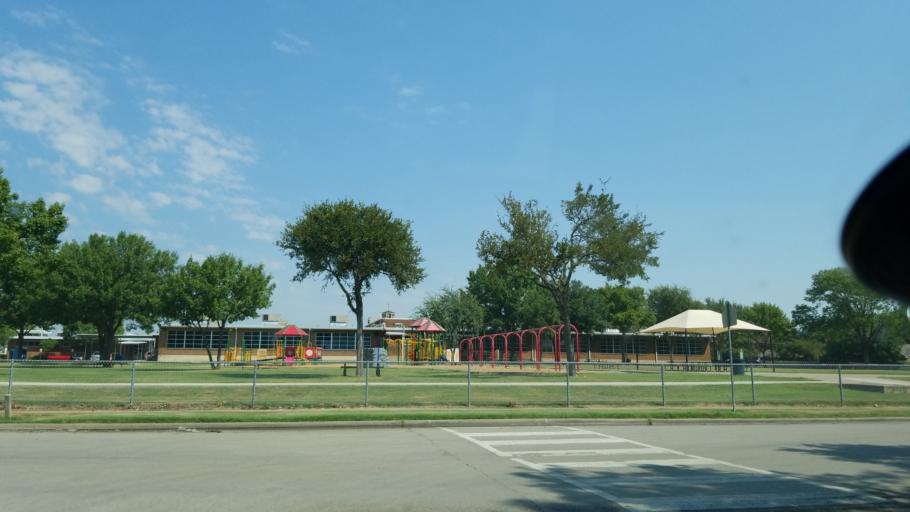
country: US
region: Texas
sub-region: Dallas County
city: Richardson
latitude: 32.8750
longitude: -96.7095
